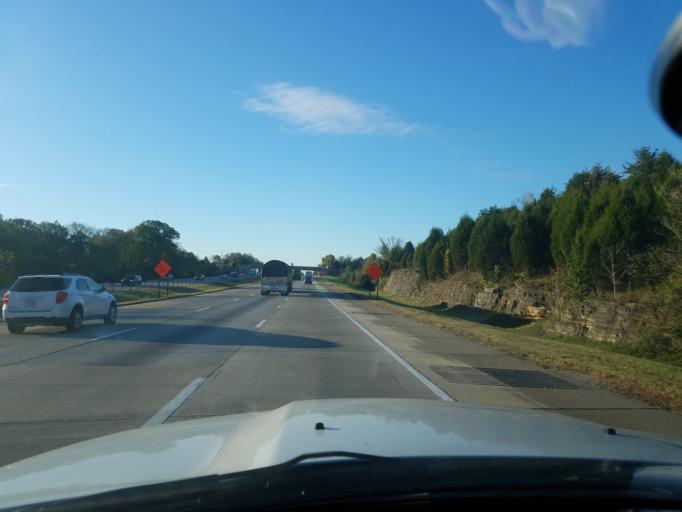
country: US
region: Kentucky
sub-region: Bullitt County
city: Brooks
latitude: 38.0267
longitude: -85.6968
